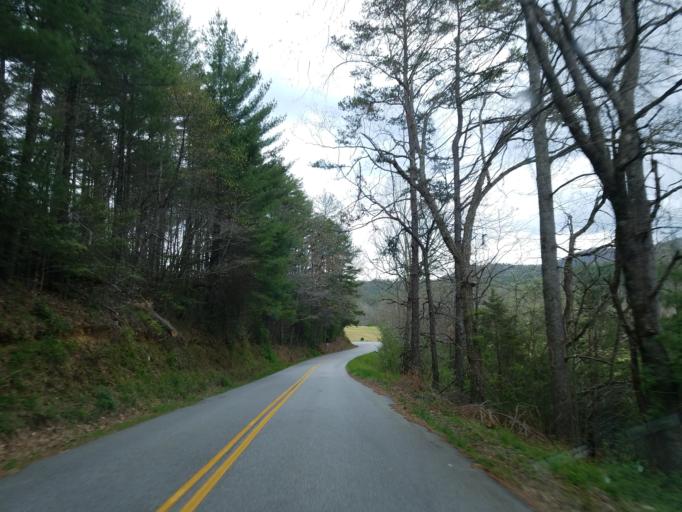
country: US
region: Georgia
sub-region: Union County
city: Blairsville
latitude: 34.7499
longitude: -84.1177
